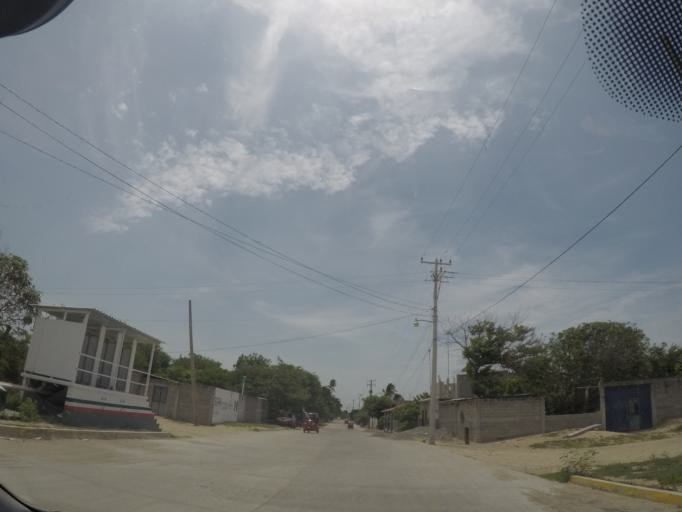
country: MX
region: Oaxaca
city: San Mateo del Mar
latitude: 16.2104
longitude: -94.9876
